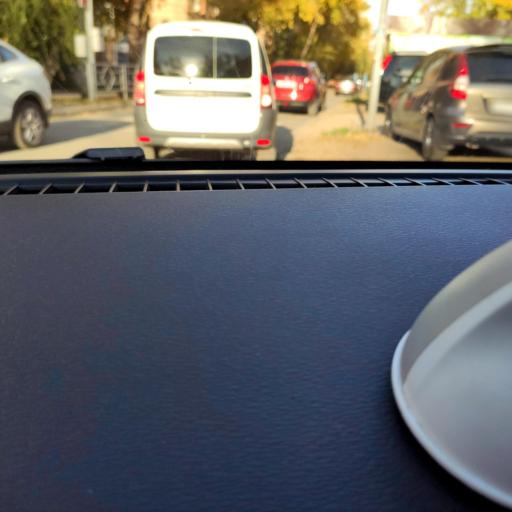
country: RU
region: Samara
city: Samara
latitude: 53.2141
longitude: 50.1626
